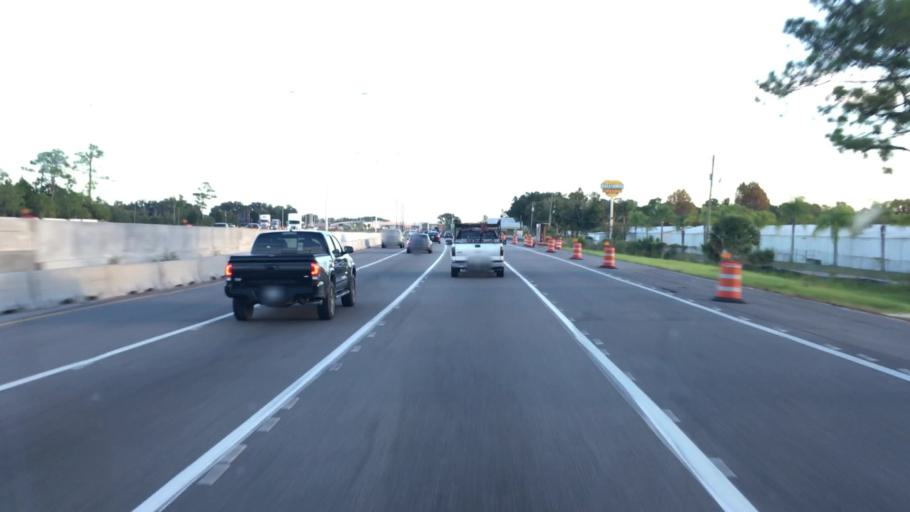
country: US
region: Florida
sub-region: Volusia County
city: Daytona Beach
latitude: 29.1672
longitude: -81.0827
